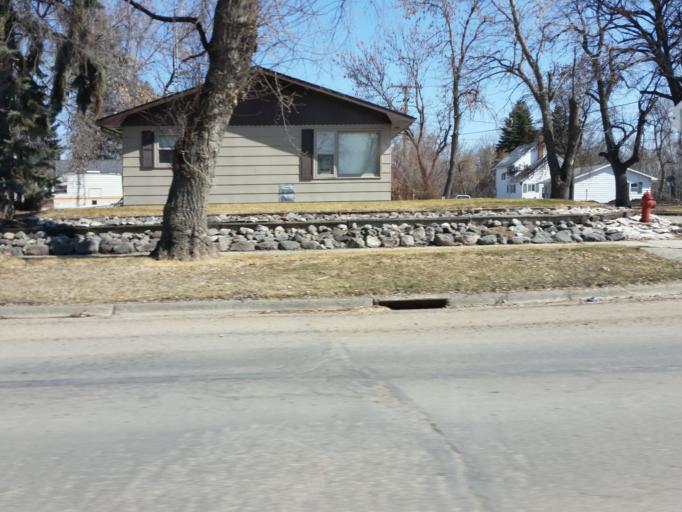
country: US
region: North Dakota
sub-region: Walsh County
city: Grafton
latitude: 48.2873
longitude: -97.3713
